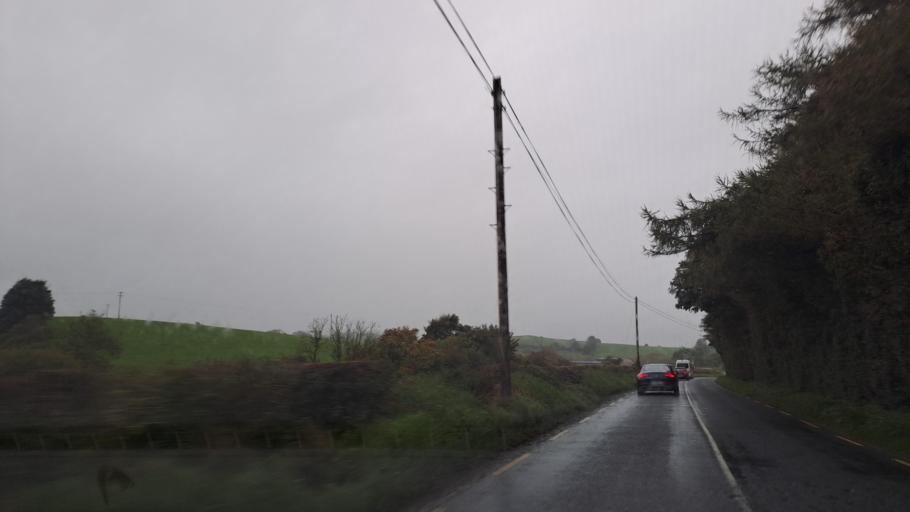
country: IE
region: Ulster
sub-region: County Monaghan
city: Monaghan
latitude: 54.2260
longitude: -6.9502
